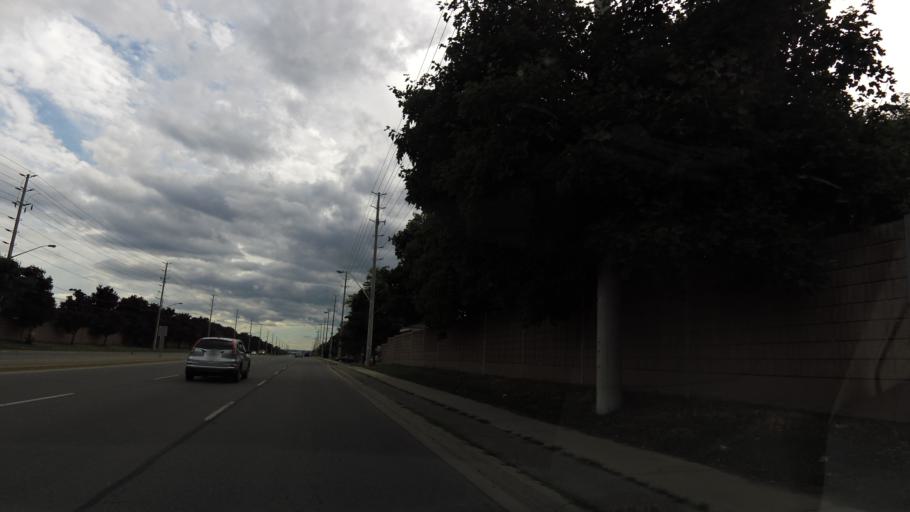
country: CA
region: Ontario
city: Brampton
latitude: 43.6529
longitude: -79.7478
